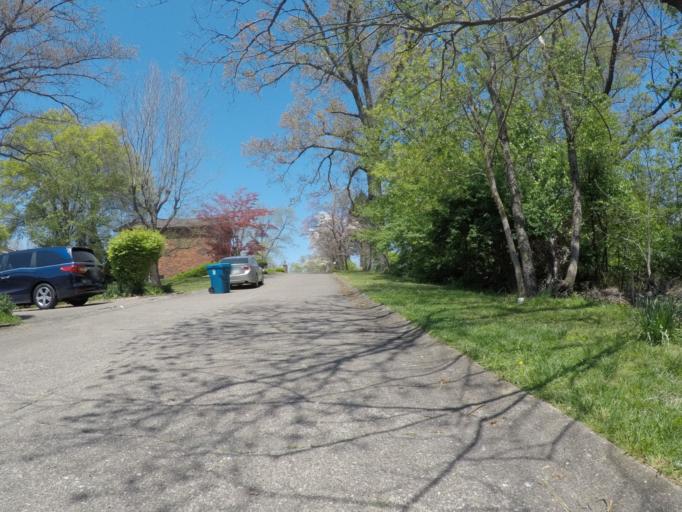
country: US
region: West Virginia
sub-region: Cabell County
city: Pea Ridge
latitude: 38.4079
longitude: -82.3456
